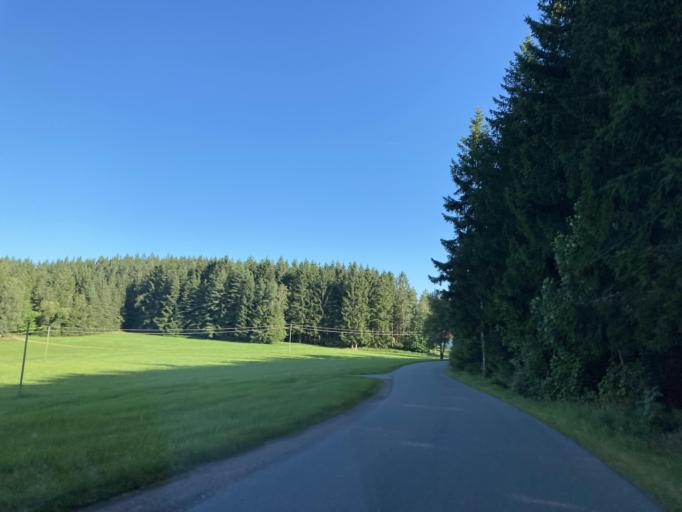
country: DE
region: Baden-Wuerttemberg
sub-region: Freiburg Region
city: Sankt Georgen im Schwarzwald
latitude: 48.1416
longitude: 8.2871
